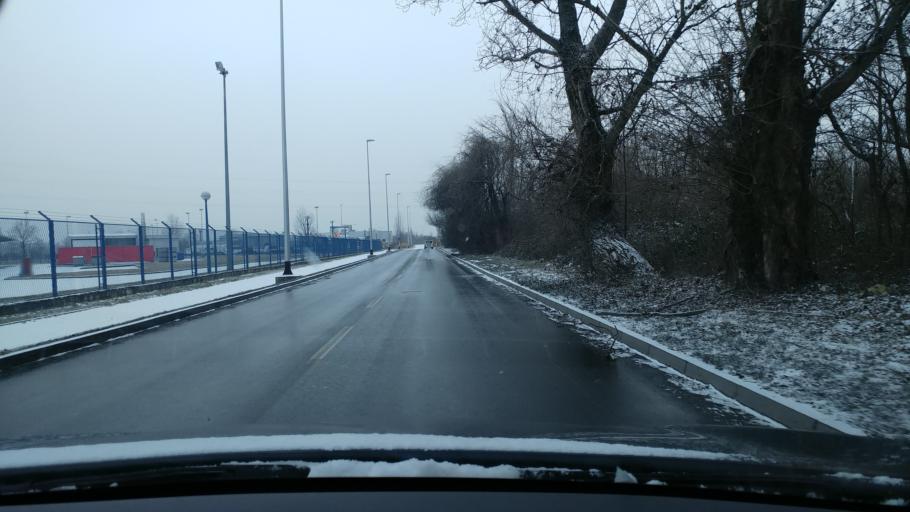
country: HR
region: Grad Zagreb
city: Stenjevec
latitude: 45.8006
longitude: 15.8730
